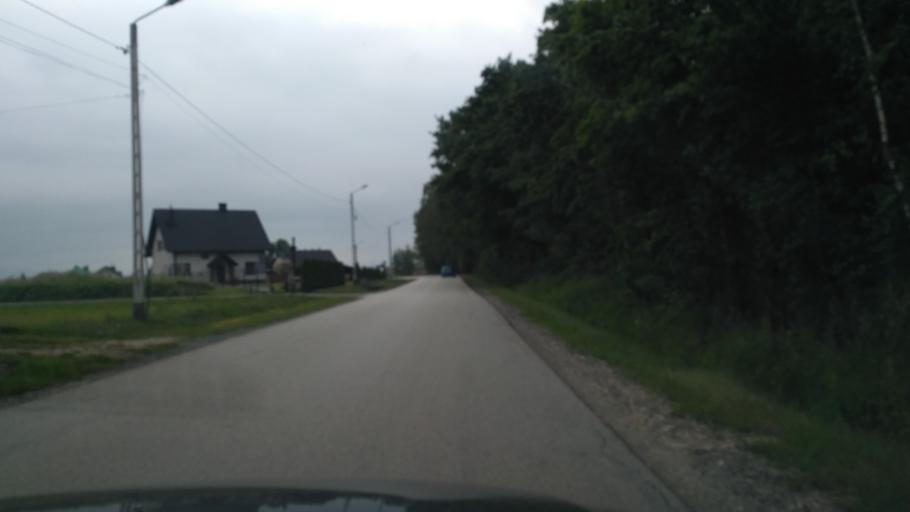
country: PL
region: Subcarpathian Voivodeship
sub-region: Powiat ropczycko-sedziszowski
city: Sedziszow Malopolski
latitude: 50.1140
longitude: 21.6741
